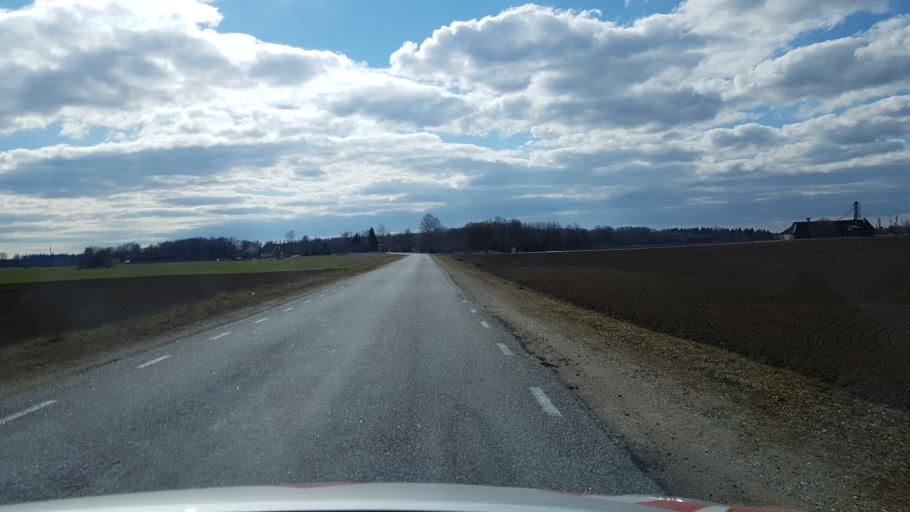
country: EE
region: Laeaene-Virumaa
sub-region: Rakvere linn
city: Rakvere
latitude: 59.3279
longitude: 26.2792
